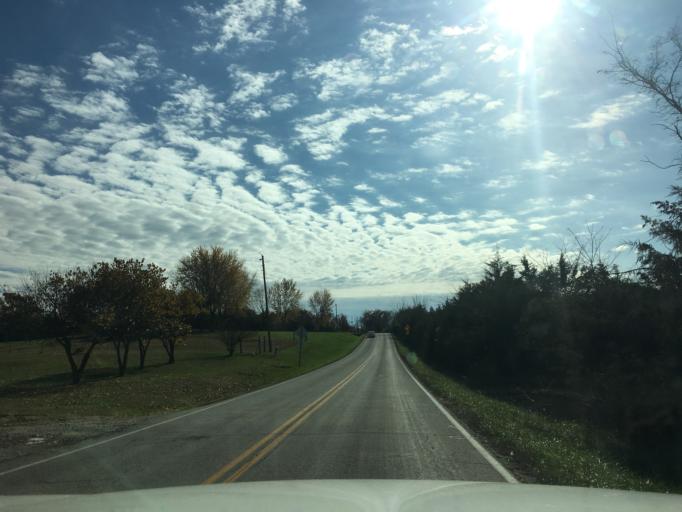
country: US
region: Missouri
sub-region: Osage County
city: Linn
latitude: 38.4240
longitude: -91.8247
